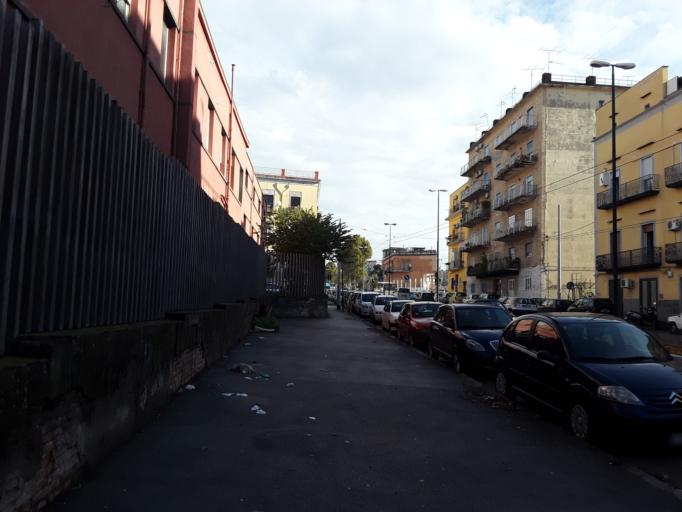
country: IT
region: Campania
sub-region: Provincia di Napoli
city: Napoli
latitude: 40.8642
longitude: 14.2683
